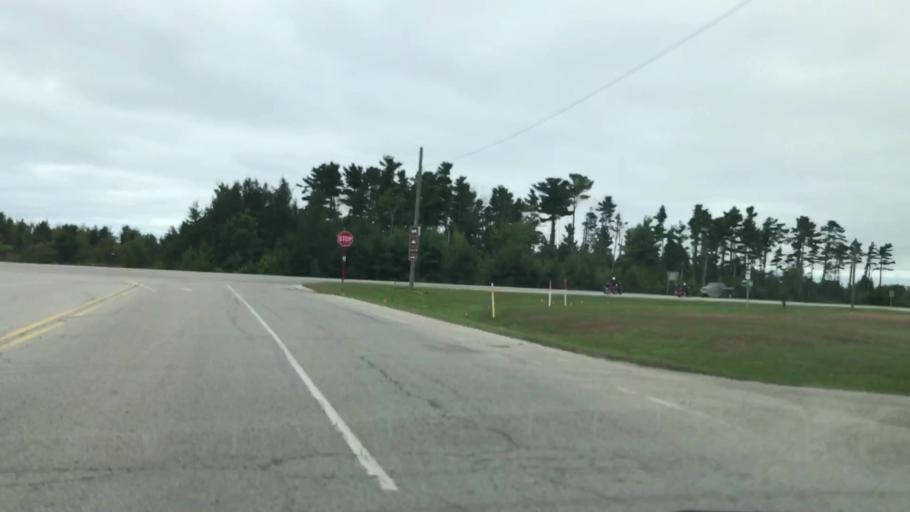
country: US
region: Michigan
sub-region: Schoolcraft County
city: Manistique
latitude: 45.9503
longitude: -86.2594
